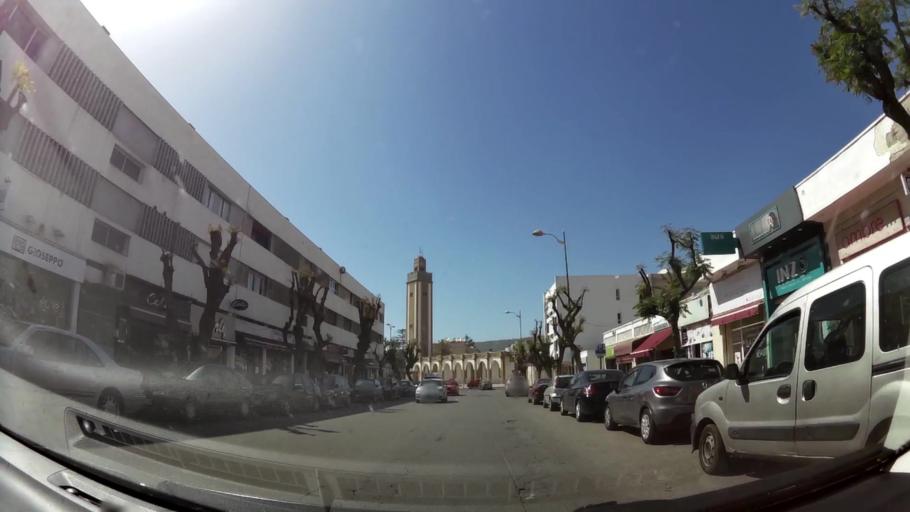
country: MA
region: Souss-Massa-Draa
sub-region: Agadir-Ida-ou-Tnan
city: Agadir
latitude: 30.4228
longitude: -9.5997
